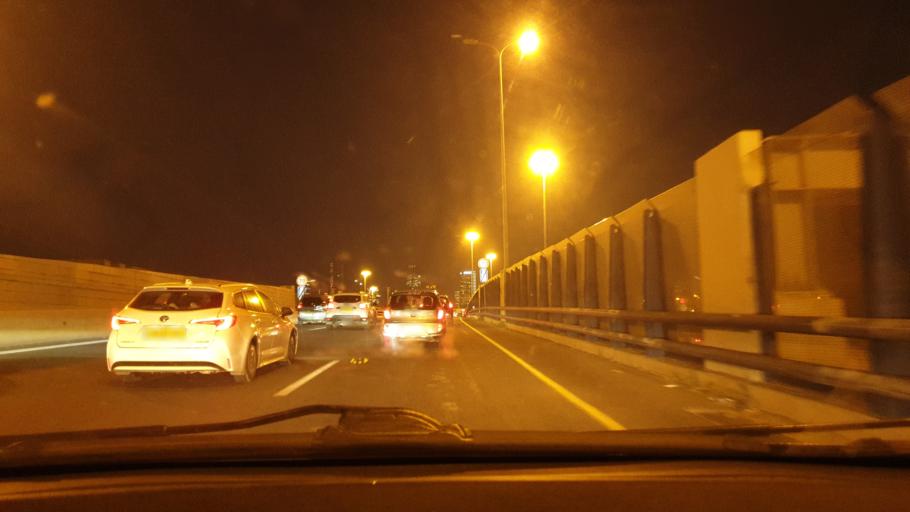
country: IL
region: Tel Aviv
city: Azor
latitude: 32.0461
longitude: 34.7837
